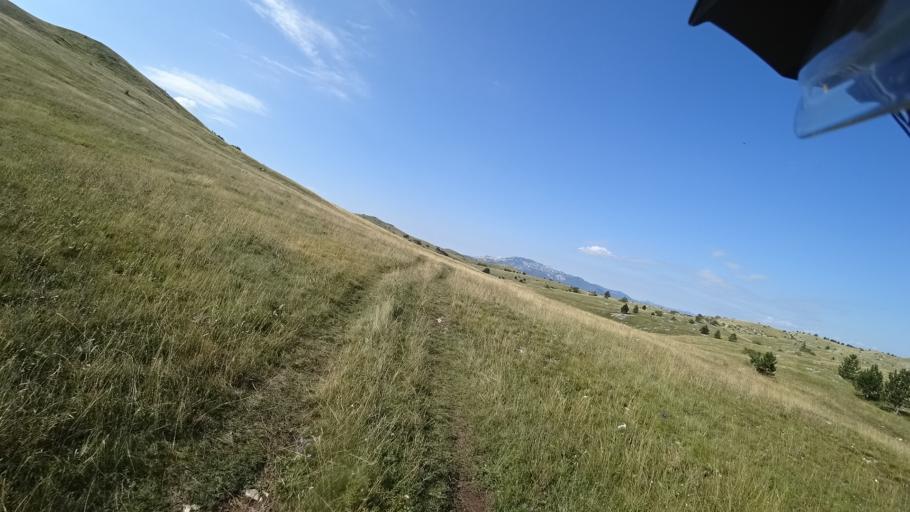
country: HR
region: Zadarska
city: Gracac
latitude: 44.3118
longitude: 15.9872
